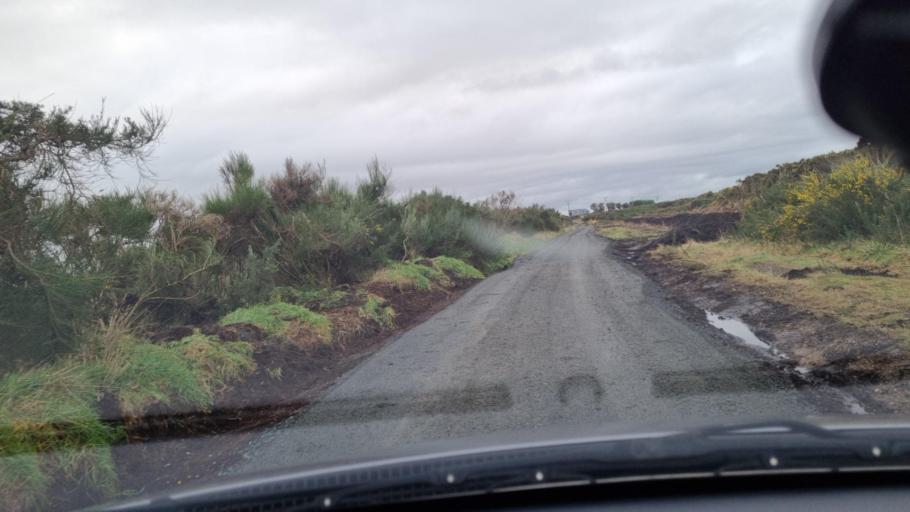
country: NZ
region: Southland
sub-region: Invercargill City
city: Bluff
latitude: -46.5409
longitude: 168.3026
